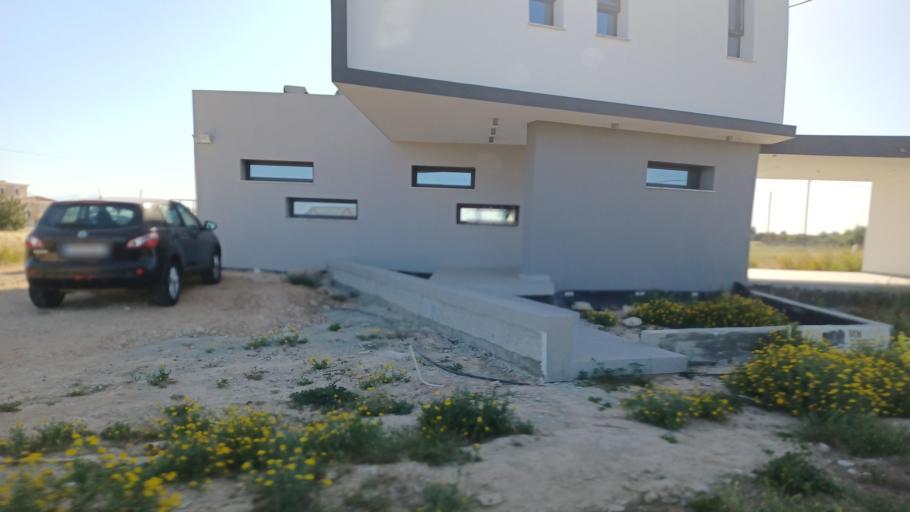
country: CY
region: Lefkosia
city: Kokkinotrimithia
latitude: 35.1449
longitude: 33.2073
